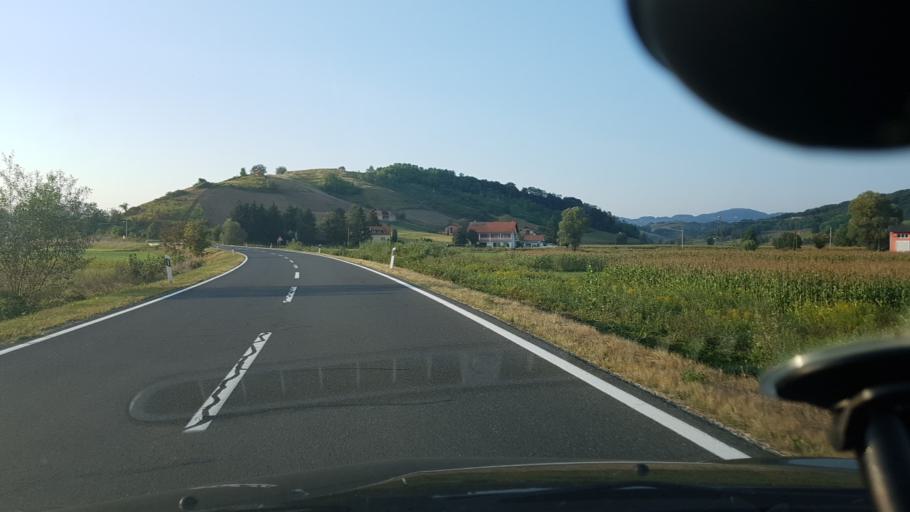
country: HR
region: Krapinsko-Zagorska
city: Pregrada
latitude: 46.1109
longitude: 15.8128
